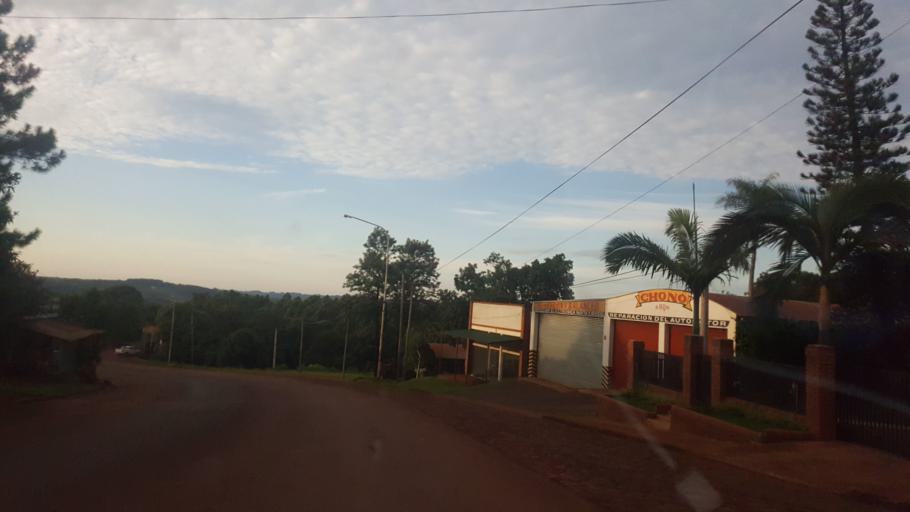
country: AR
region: Misiones
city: Dos de Mayo
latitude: -27.0271
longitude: -54.6880
